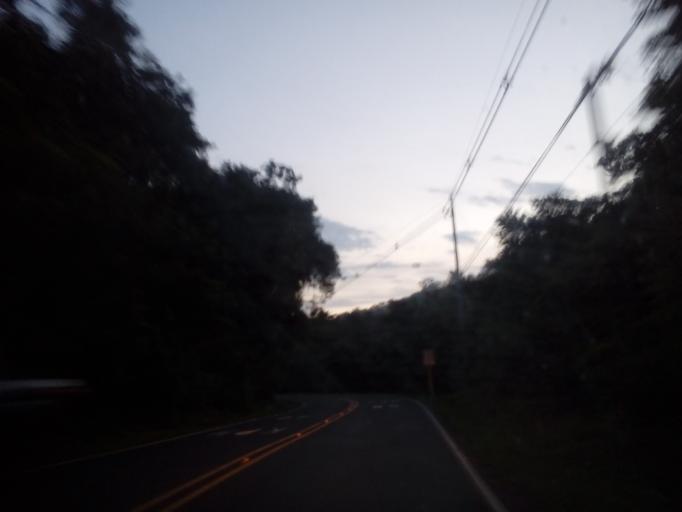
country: CR
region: Guanacaste
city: Samara
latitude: 9.9495
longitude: -85.5183
